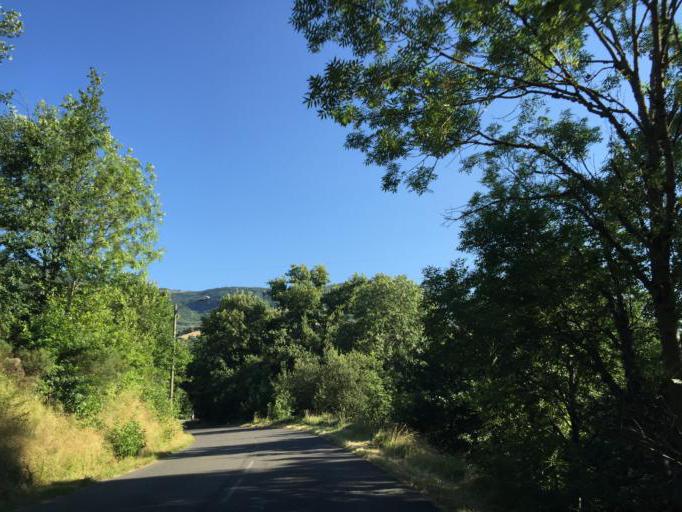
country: FR
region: Rhone-Alpes
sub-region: Departement de la Loire
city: Saint-Jean-Bonnefonds
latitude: 45.4469
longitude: 4.4805
